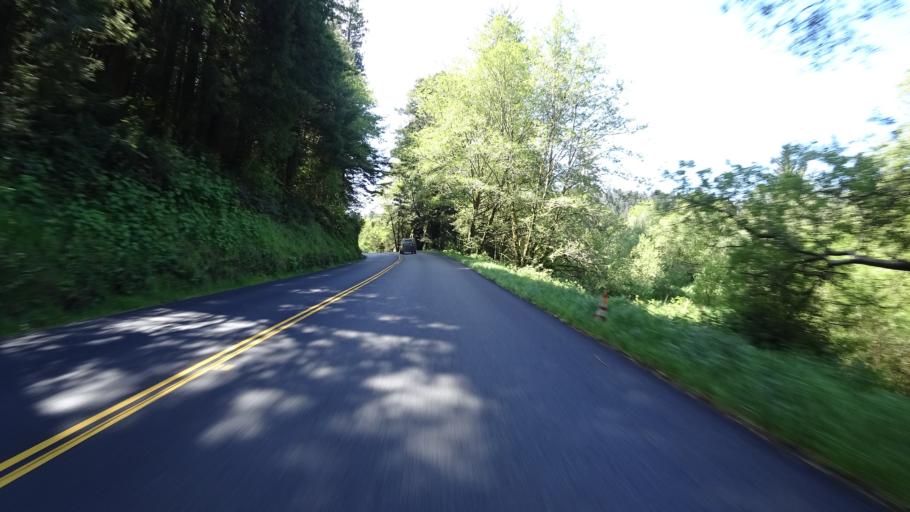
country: US
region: California
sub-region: Humboldt County
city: Westhaven-Moonstone
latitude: 41.3114
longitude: -124.0452
